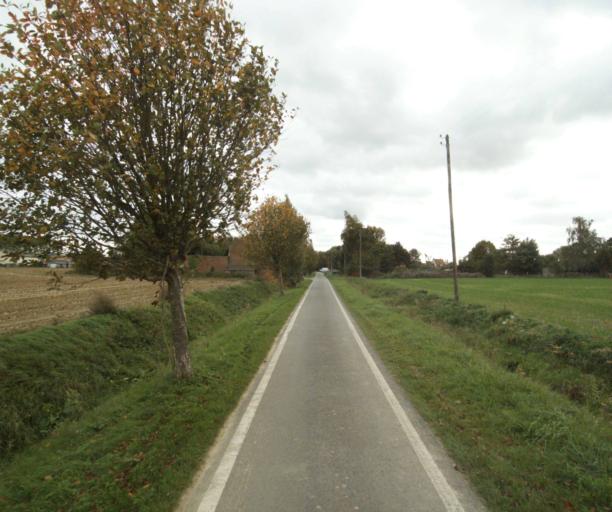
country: FR
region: Nord-Pas-de-Calais
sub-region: Departement du Nord
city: Bois-Grenier
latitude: 50.6583
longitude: 2.9082
